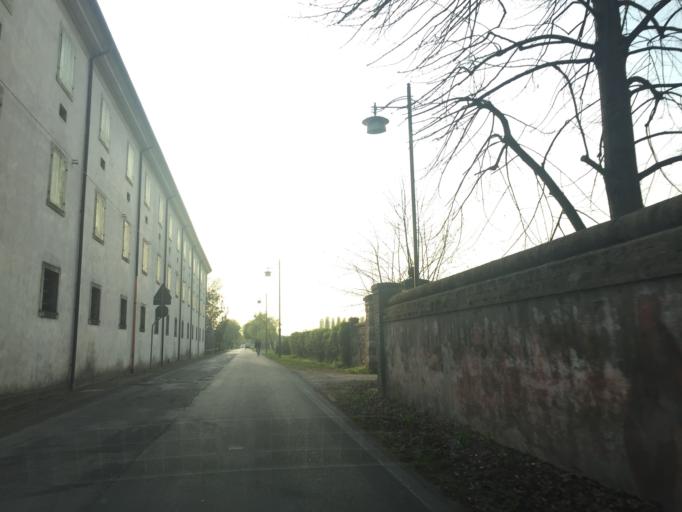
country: IT
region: Friuli Venezia Giulia
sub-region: Provincia di Pordenone
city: Cavolano-Schiavoi
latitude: 45.9365
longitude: 12.4734
